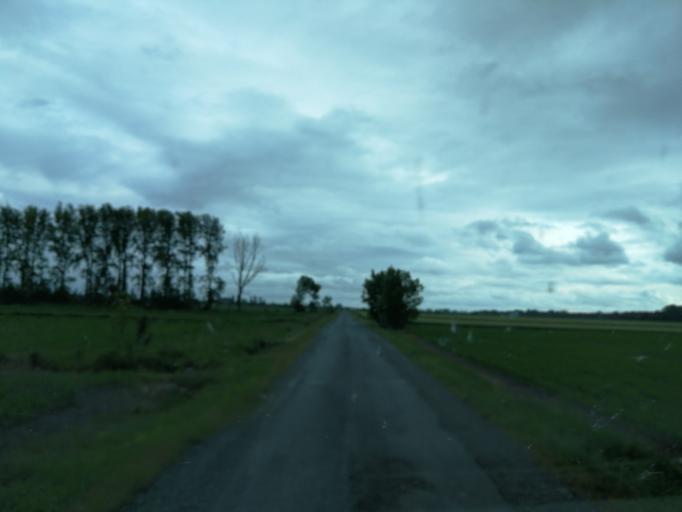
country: FR
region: Pays de la Loire
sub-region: Departement de la Vendee
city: Vix
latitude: 46.3666
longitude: -0.9338
